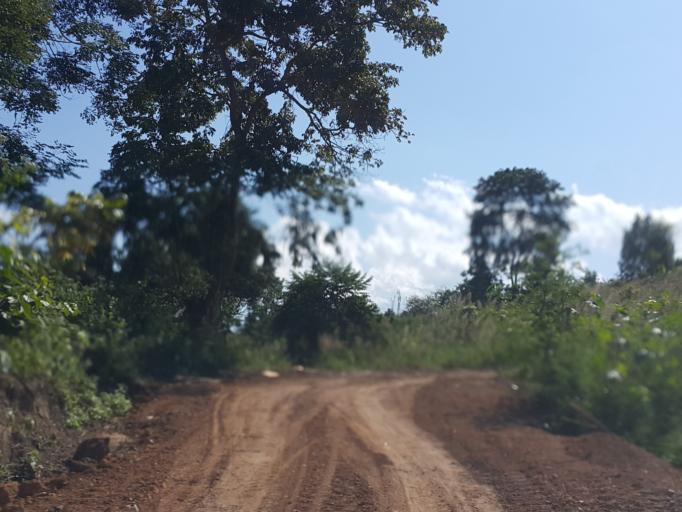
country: TH
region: Chiang Mai
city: Mae Taeng
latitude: 18.9578
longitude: 98.9021
